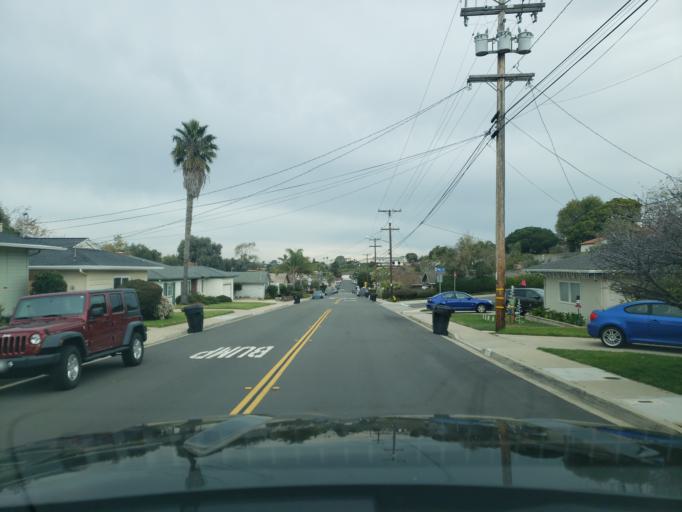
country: US
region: California
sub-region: San Diego County
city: Coronado
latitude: 32.7225
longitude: -117.2417
